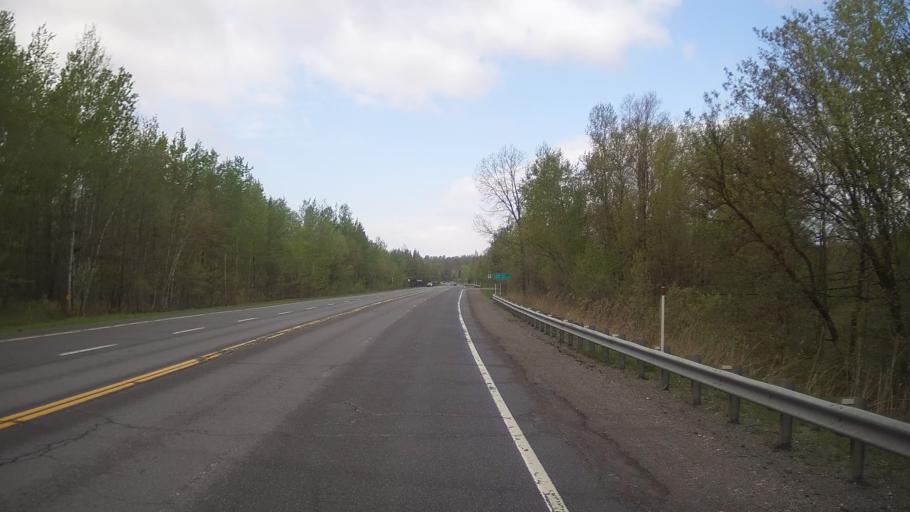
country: CA
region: Quebec
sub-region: Monteregie
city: Cowansville
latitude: 45.1987
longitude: -72.7185
